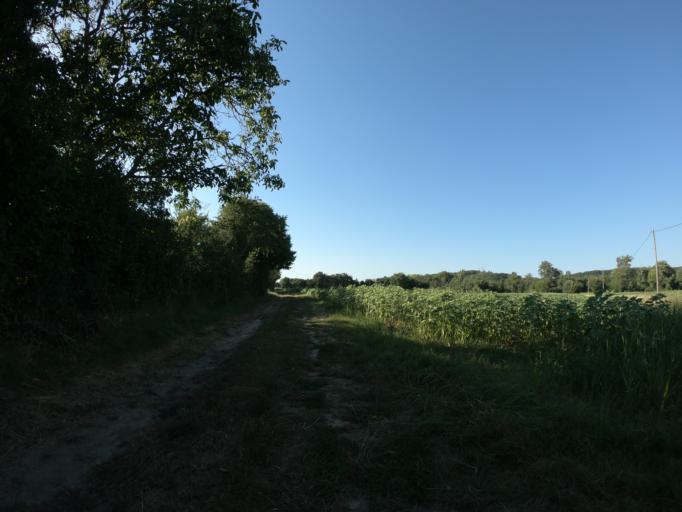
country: FR
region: Midi-Pyrenees
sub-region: Departement de l'Ariege
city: La Tour-du-Crieu
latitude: 43.0975
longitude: 1.7414
